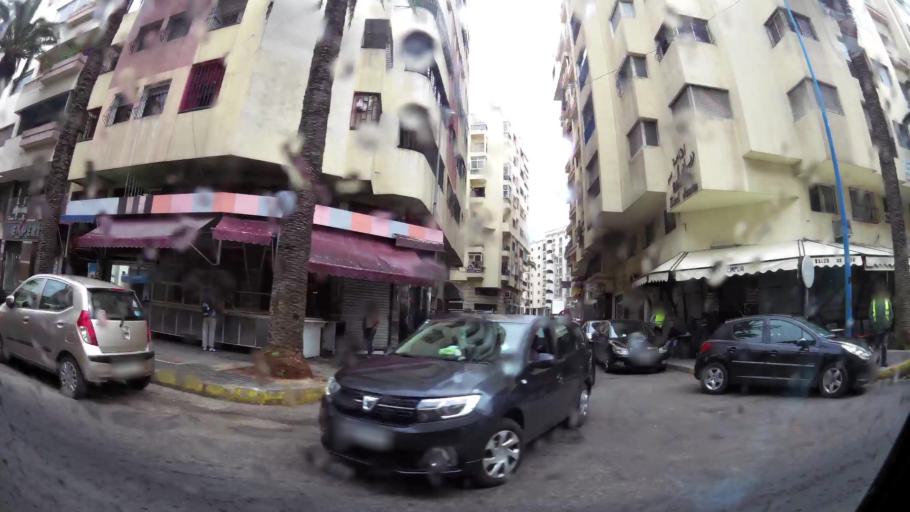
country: MA
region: Grand Casablanca
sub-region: Casablanca
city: Casablanca
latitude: 33.6012
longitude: -7.6382
